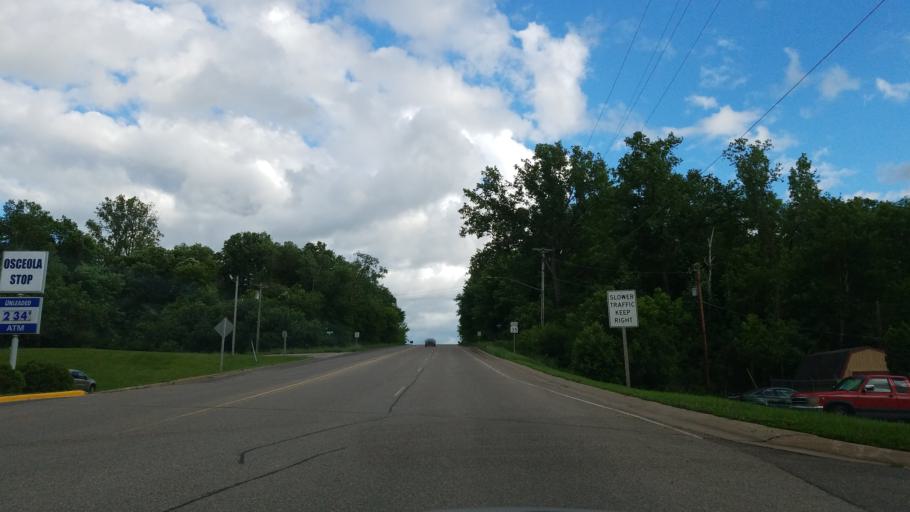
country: US
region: Wisconsin
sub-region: Polk County
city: Osceola
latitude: 45.3184
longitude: -92.7052
